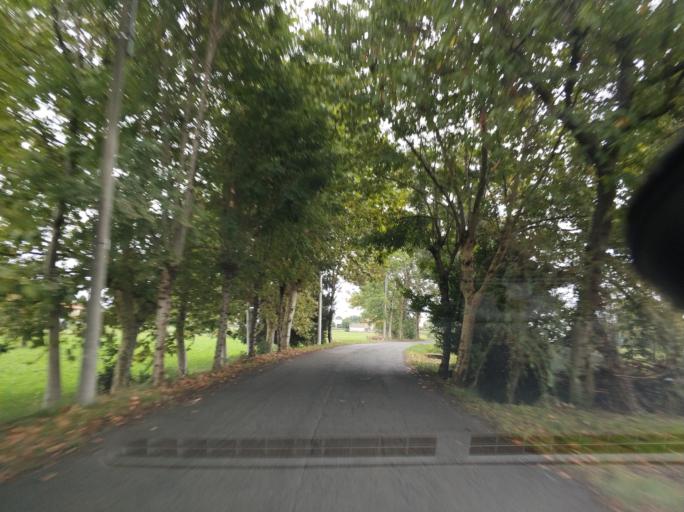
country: IT
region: Piedmont
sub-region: Provincia di Torino
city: Cirie
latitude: 45.2159
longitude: 7.6026
